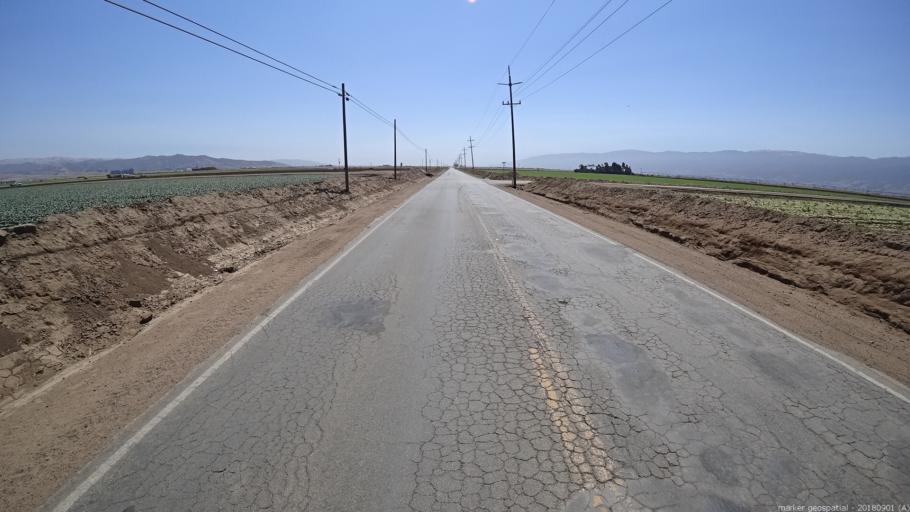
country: US
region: California
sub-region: Monterey County
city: Chualar
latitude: 36.6050
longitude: -121.5138
